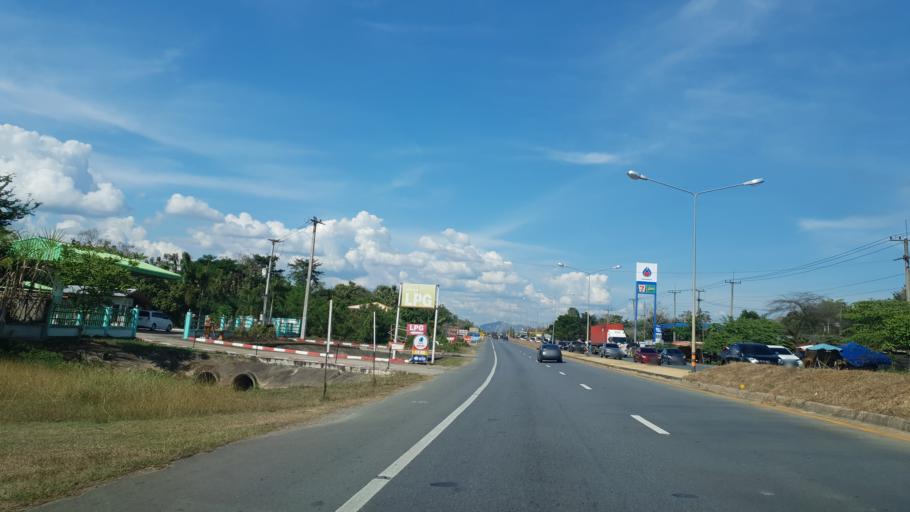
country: TH
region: Phrae
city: Den Chai
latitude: 17.9549
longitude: 100.0682
